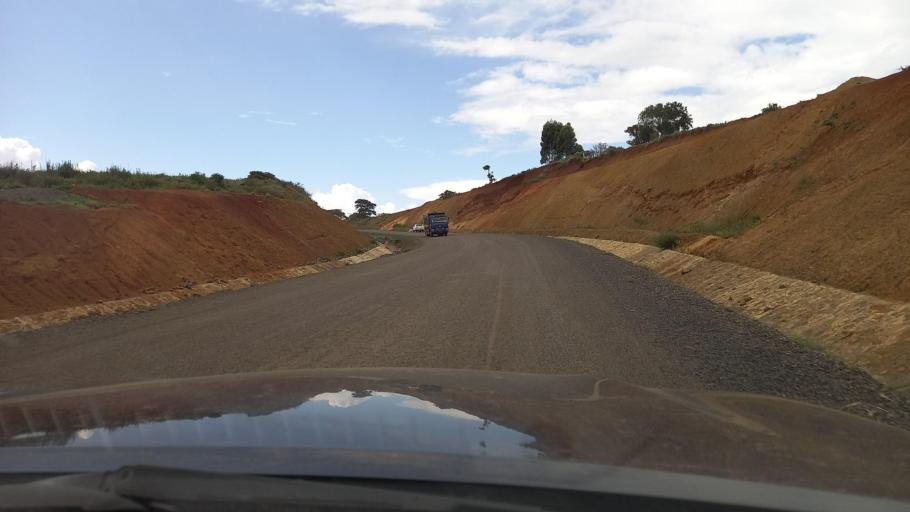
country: ET
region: Southern Nations, Nationalities, and People's Region
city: Mizan Teferi
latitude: 6.2109
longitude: 35.6421
